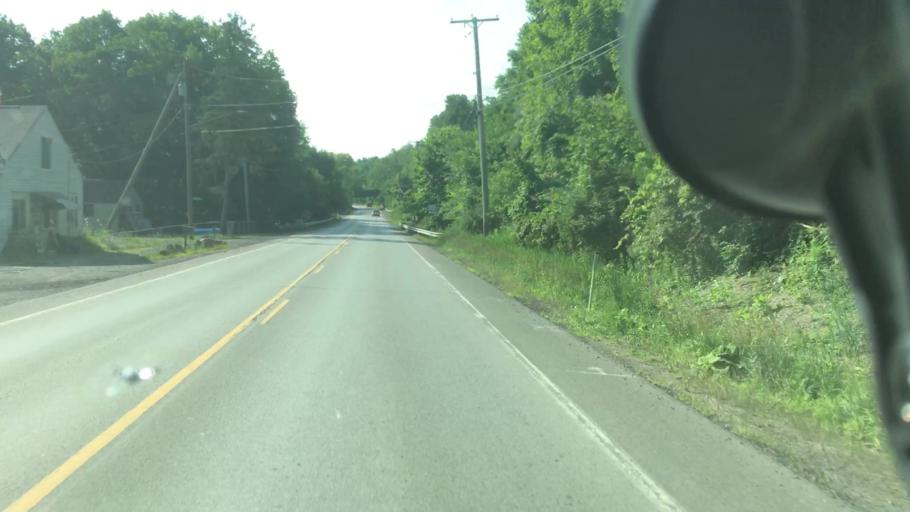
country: US
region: Pennsylvania
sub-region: Lawrence County
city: Bessemer
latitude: 41.0174
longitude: -80.4961
